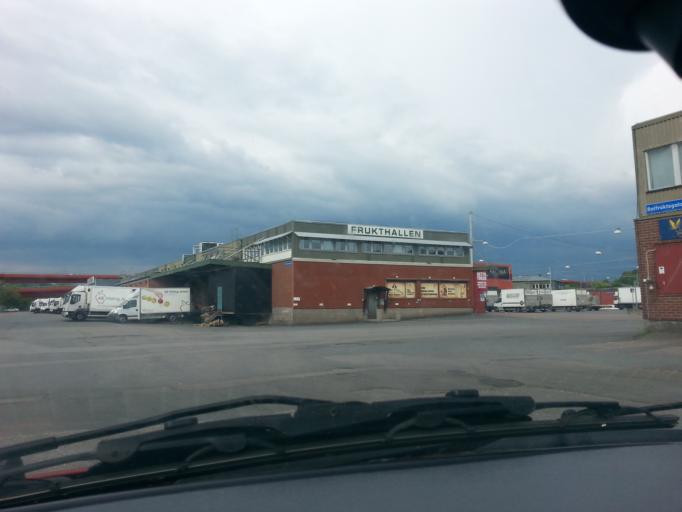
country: SE
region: Vaestra Goetaland
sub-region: Goteborg
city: Goeteborg
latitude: 57.7227
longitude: 11.9991
